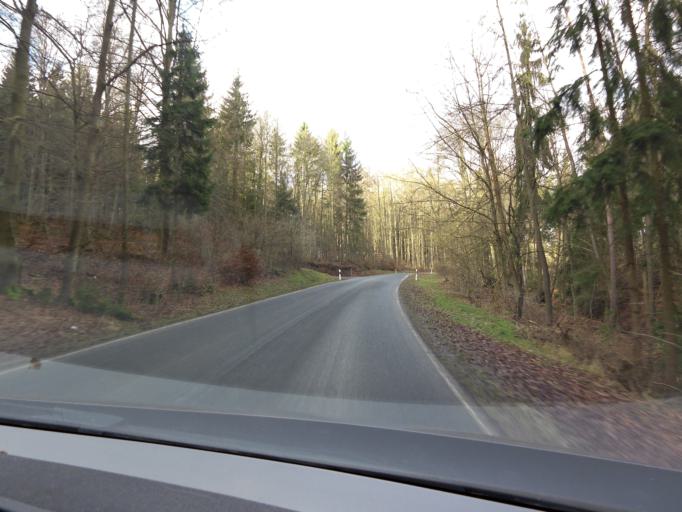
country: DE
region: Thuringia
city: Creuzburg
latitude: 51.0706
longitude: 10.2255
